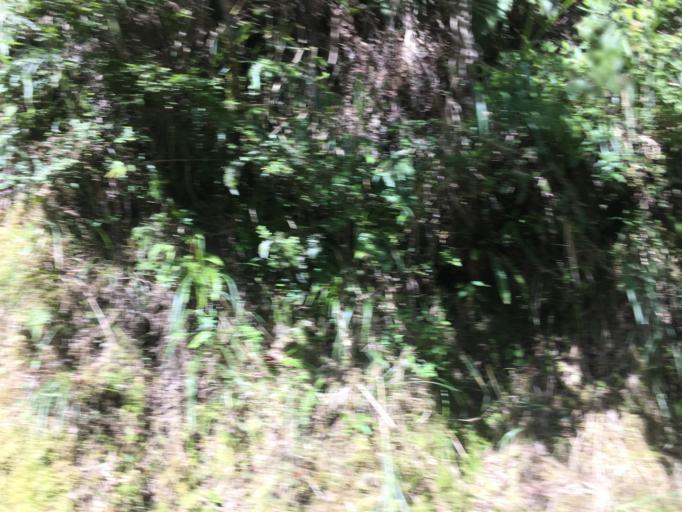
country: TW
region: Taiwan
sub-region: Yilan
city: Yilan
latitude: 24.6203
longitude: 121.4767
